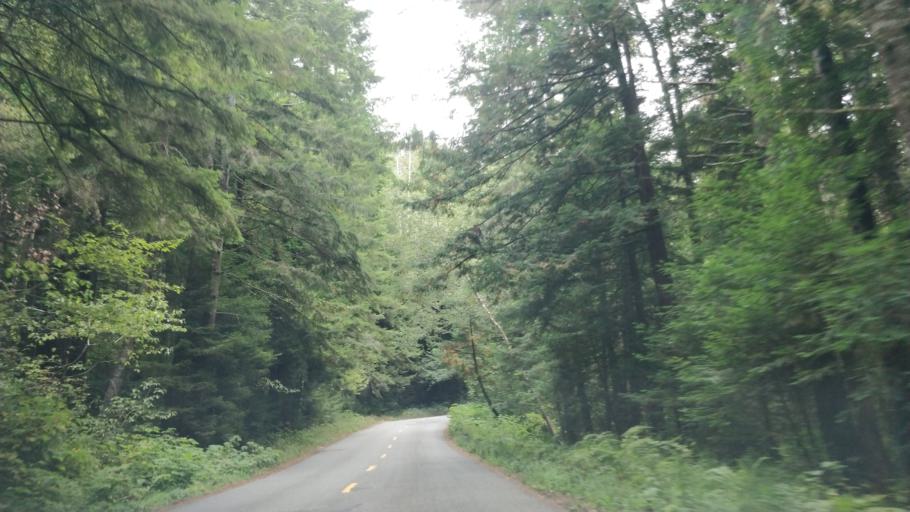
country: US
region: California
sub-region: Humboldt County
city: Westhaven-Moonstone
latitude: 41.2992
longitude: -124.0214
